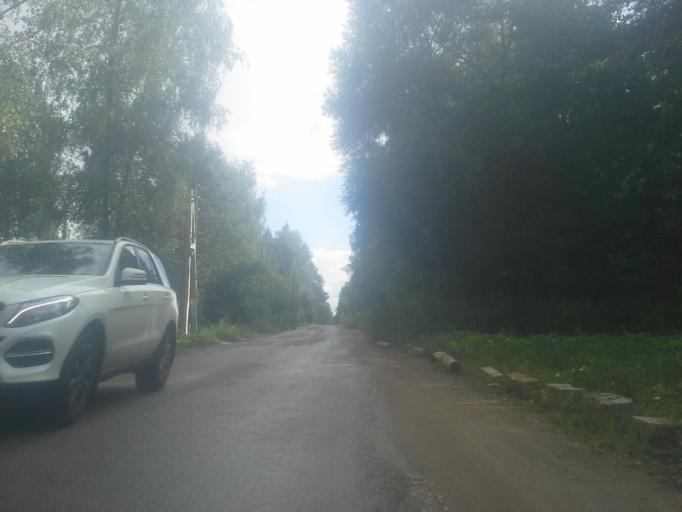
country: RU
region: Moskovskaya
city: Zhavoronki
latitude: 55.6406
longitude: 37.1450
